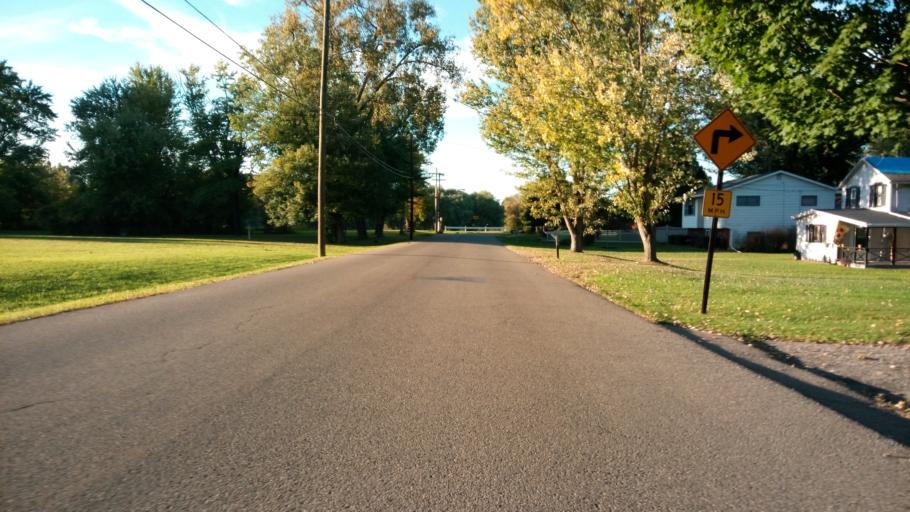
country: US
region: New York
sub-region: Chemung County
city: Elmira
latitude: 42.0767
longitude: -76.8220
